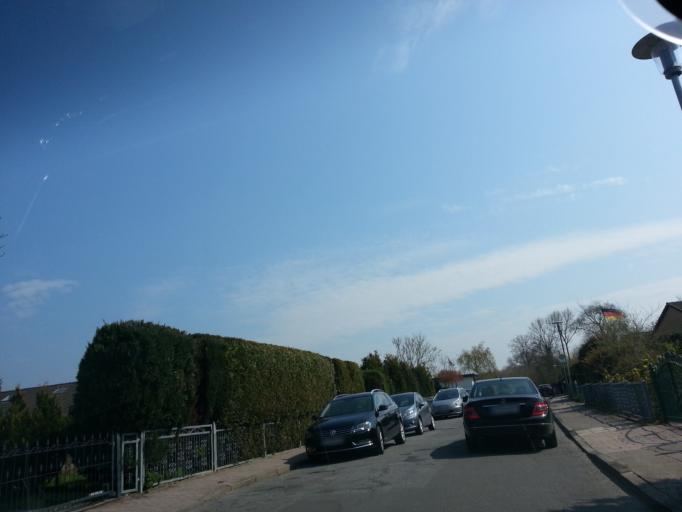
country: DE
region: Schleswig-Holstein
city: Travemuende
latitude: 53.9882
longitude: 10.8412
